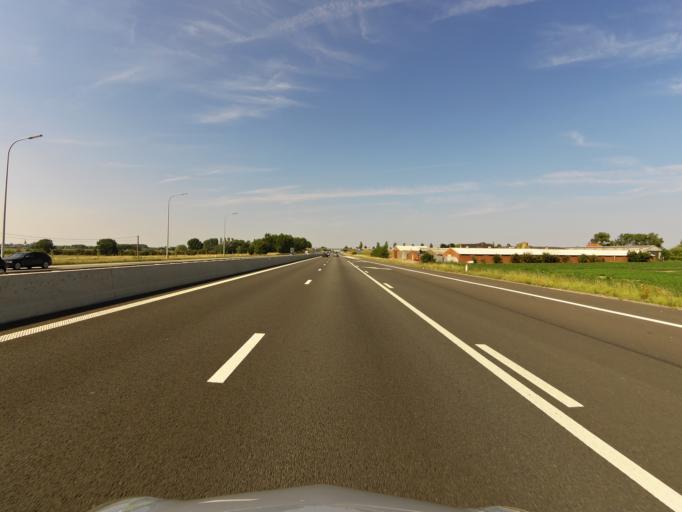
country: BE
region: Flanders
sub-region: Provincie West-Vlaanderen
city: Lichtervelde
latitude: 51.0141
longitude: 3.1699
